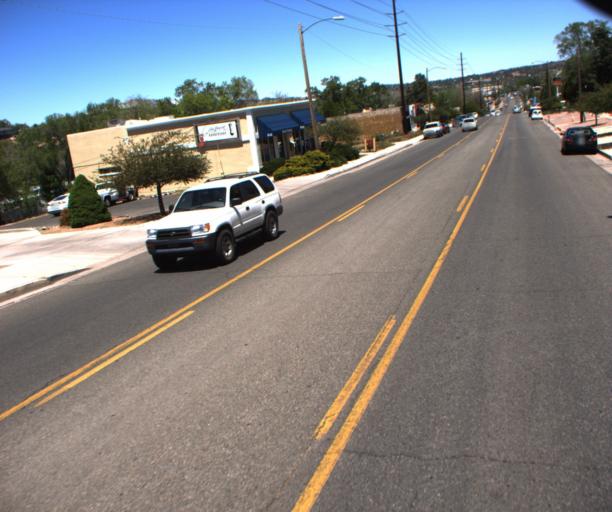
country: US
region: Arizona
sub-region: Yavapai County
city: Prescott
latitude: 34.5326
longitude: -112.4703
